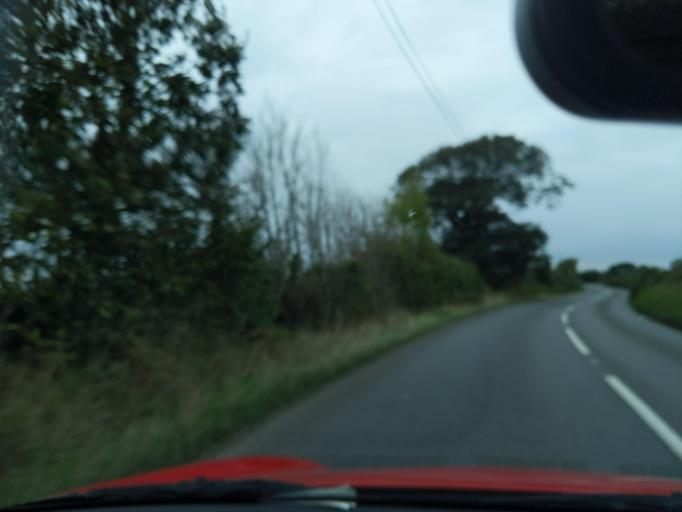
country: GB
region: England
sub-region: Devon
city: Okehampton
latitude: 50.8451
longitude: -4.0721
